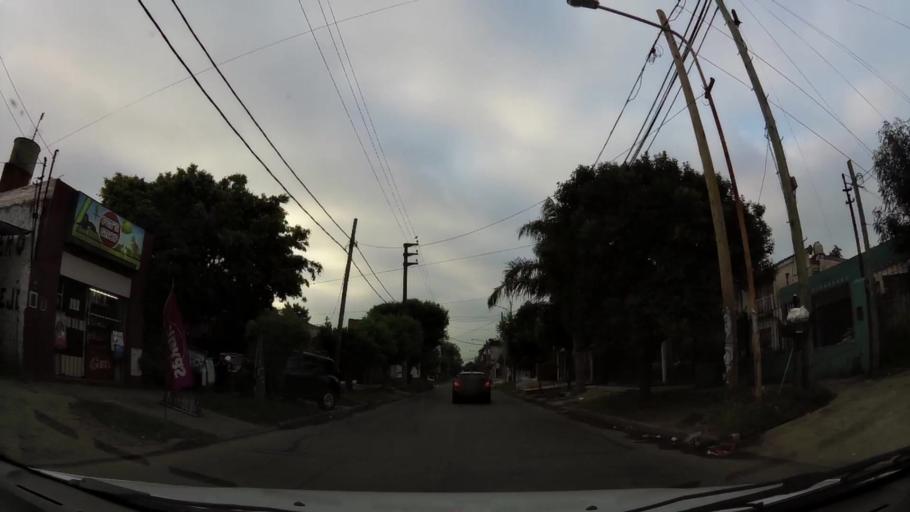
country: AR
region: Buenos Aires
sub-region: Partido de Moron
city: Moron
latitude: -34.6758
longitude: -58.6049
